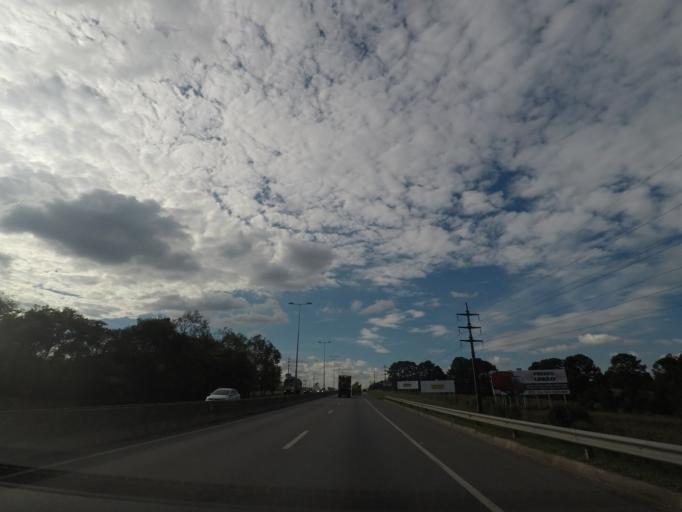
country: BR
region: Parana
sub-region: Araucaria
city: Araucaria
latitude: -25.5887
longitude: -49.3148
